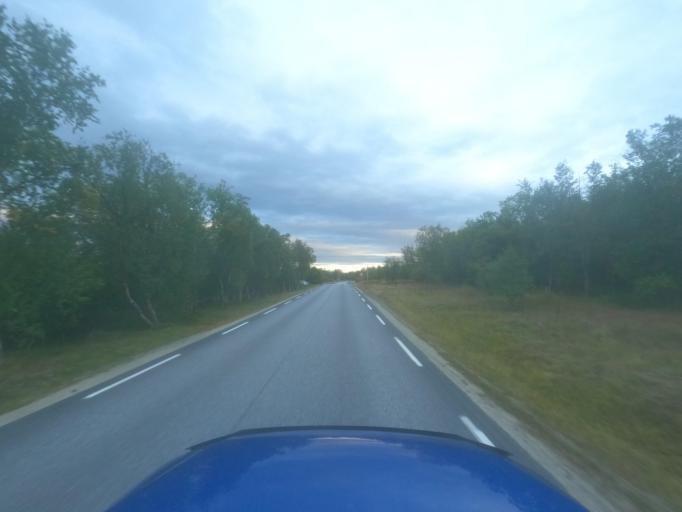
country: NO
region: Finnmark Fylke
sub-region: Porsanger
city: Lakselv
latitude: 70.1496
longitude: 24.9010
